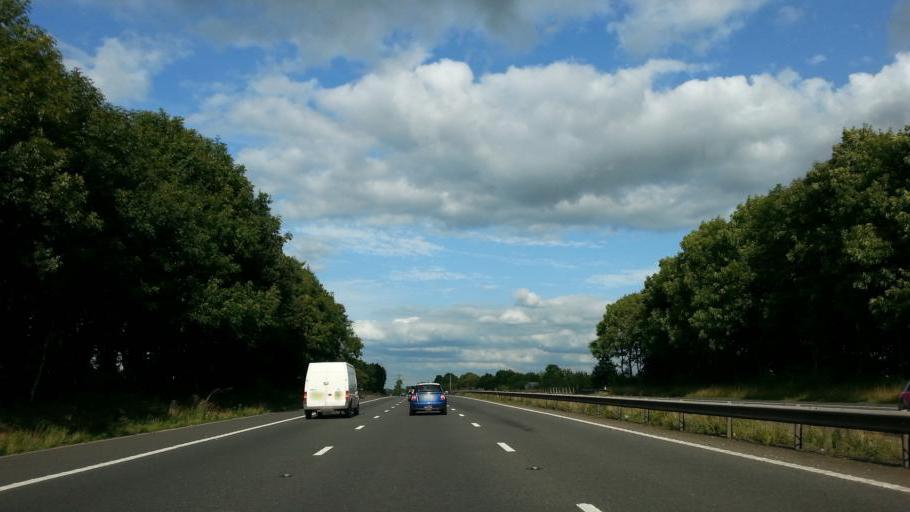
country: GB
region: England
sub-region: Leicestershire
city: Hinckley
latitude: 52.5151
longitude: -1.3617
